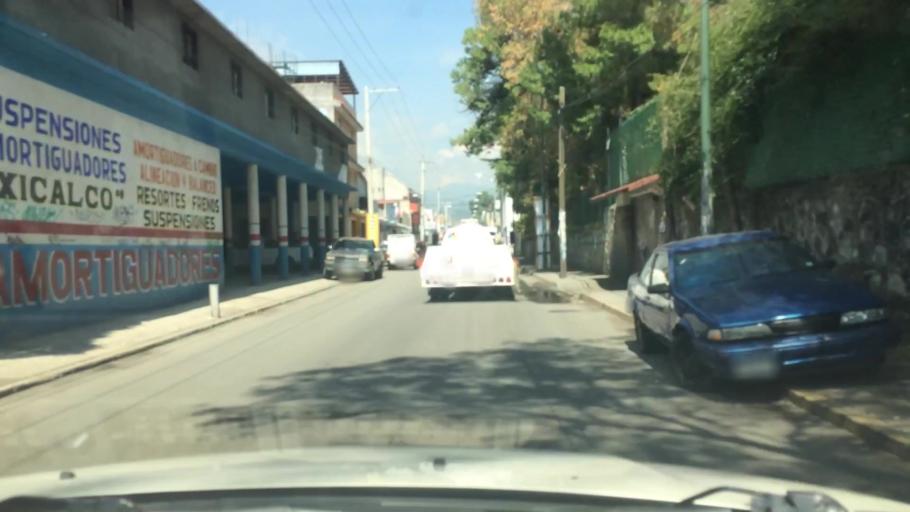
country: MX
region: Mexico City
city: Tlalpan
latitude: 19.2344
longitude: -99.1673
